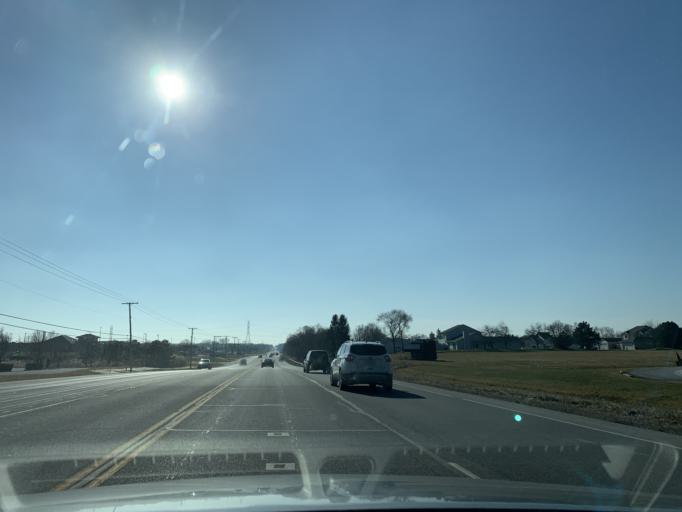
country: US
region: Indiana
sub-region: Lake County
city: Saint John
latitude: 41.4406
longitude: -87.4700
